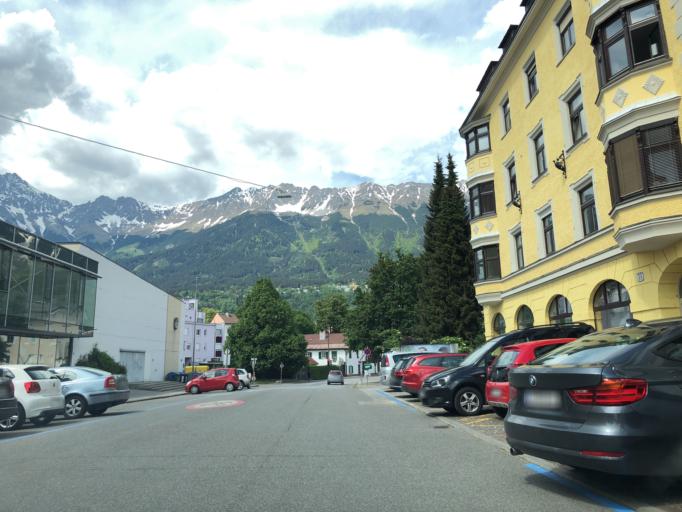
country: AT
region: Tyrol
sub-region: Innsbruck Stadt
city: Innsbruck
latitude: 47.2670
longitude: 11.4085
